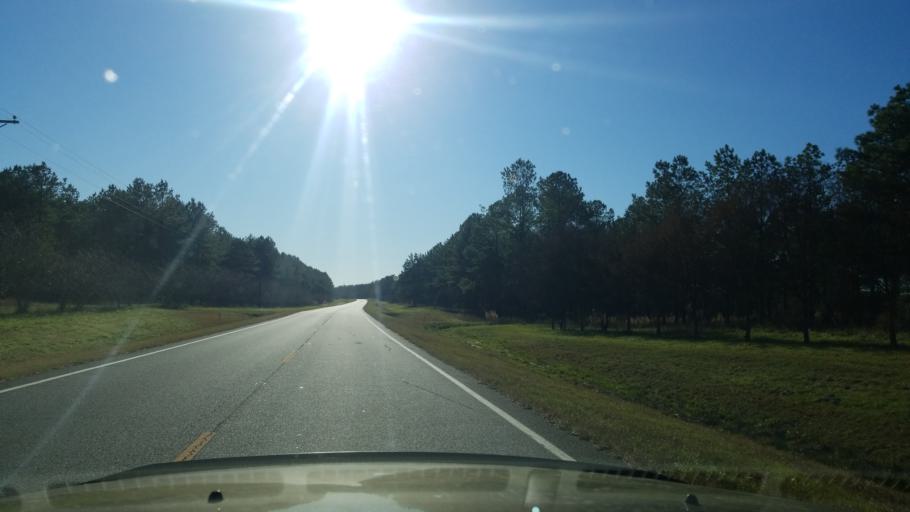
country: US
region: Georgia
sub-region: Talbot County
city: Talbotton
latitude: 32.6242
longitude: -84.5401
